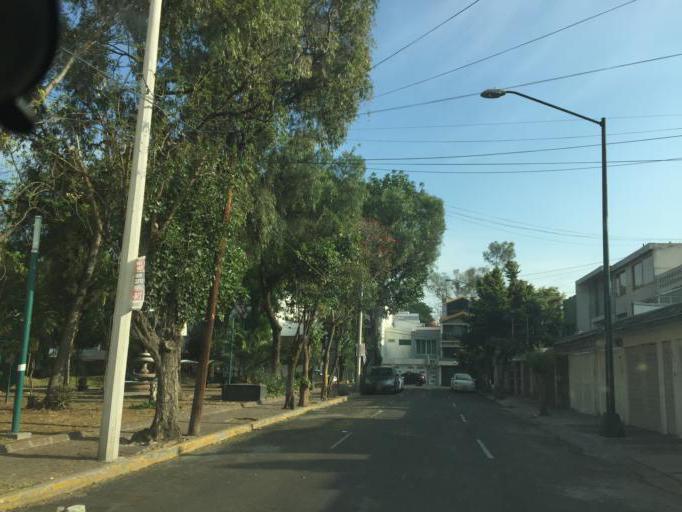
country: MX
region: Mexico
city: Colonia Lindavista
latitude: 19.4935
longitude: -99.1352
